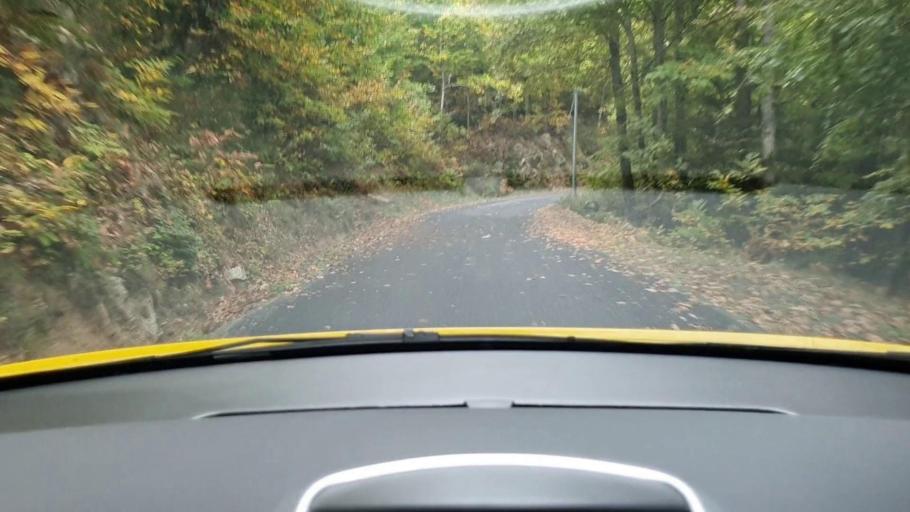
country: FR
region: Languedoc-Roussillon
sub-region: Departement de la Lozere
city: Meyrueis
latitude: 44.0627
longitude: 3.4385
